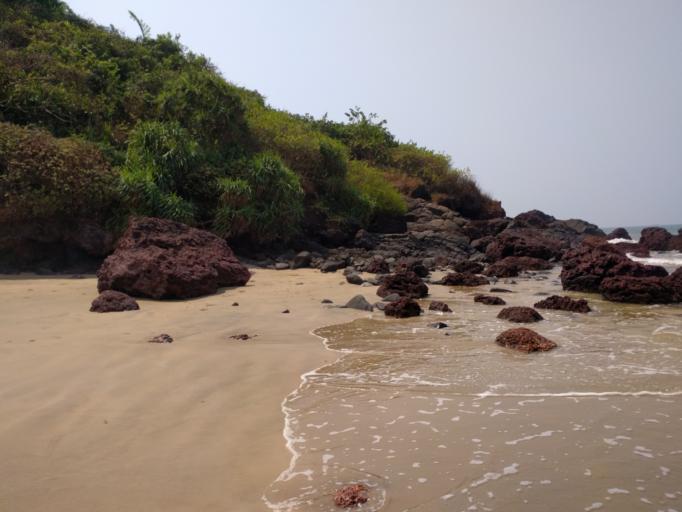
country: IN
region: Karnataka
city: Canacona
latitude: 14.9737
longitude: 74.0434
